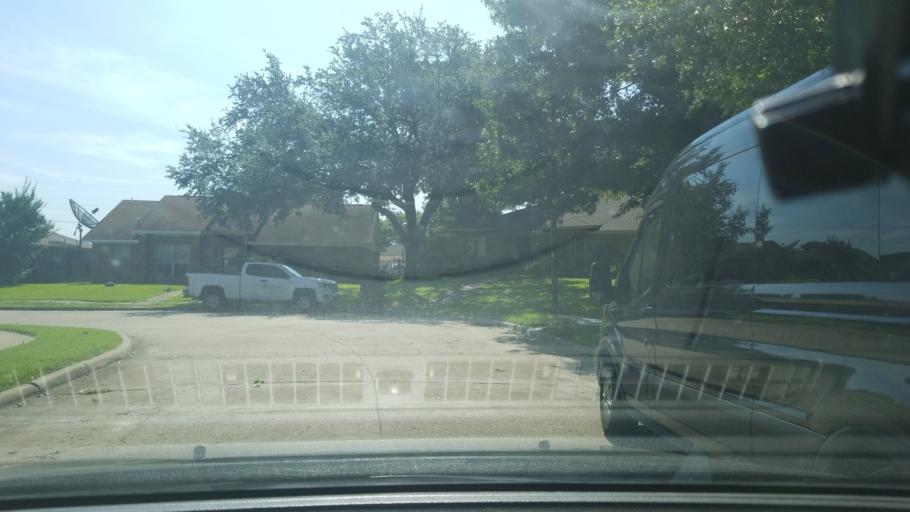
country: US
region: Texas
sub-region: Dallas County
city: Mesquite
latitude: 32.7767
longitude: -96.5920
